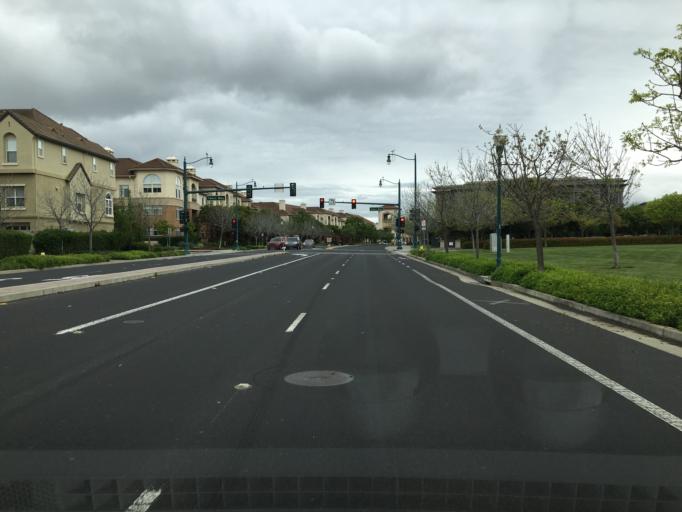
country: US
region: California
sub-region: San Mateo County
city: Foster City
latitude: 37.5458
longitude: -122.2951
